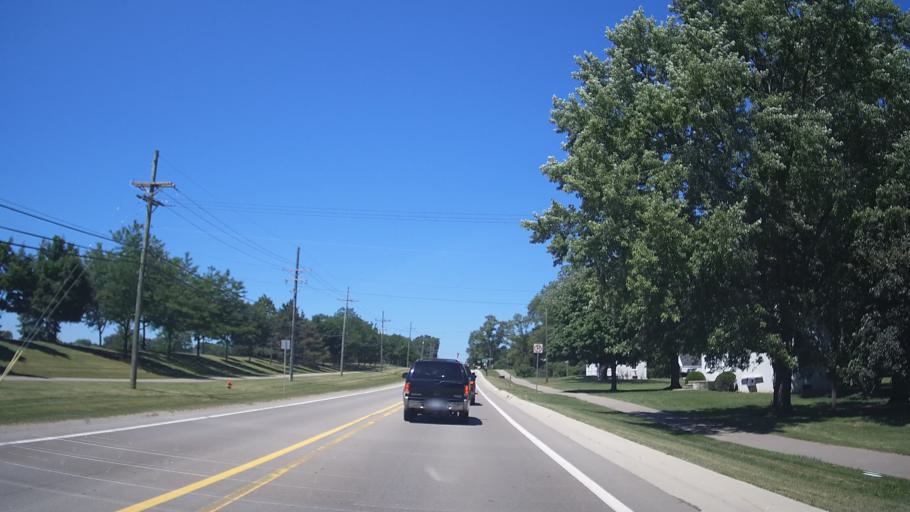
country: US
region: Michigan
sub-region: Oakland County
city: Rochester
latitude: 42.6531
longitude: -83.1070
